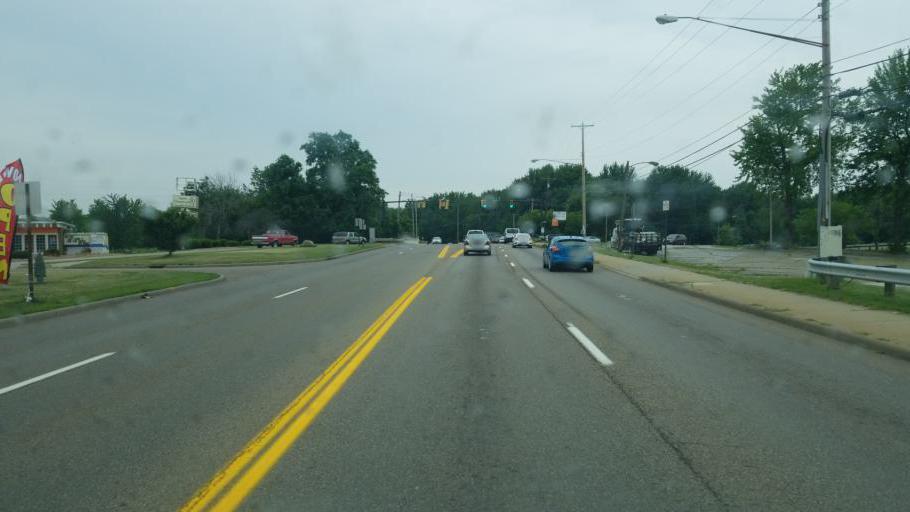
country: US
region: Ohio
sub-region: Summit County
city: Portage Lakes
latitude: 41.0249
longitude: -81.5490
